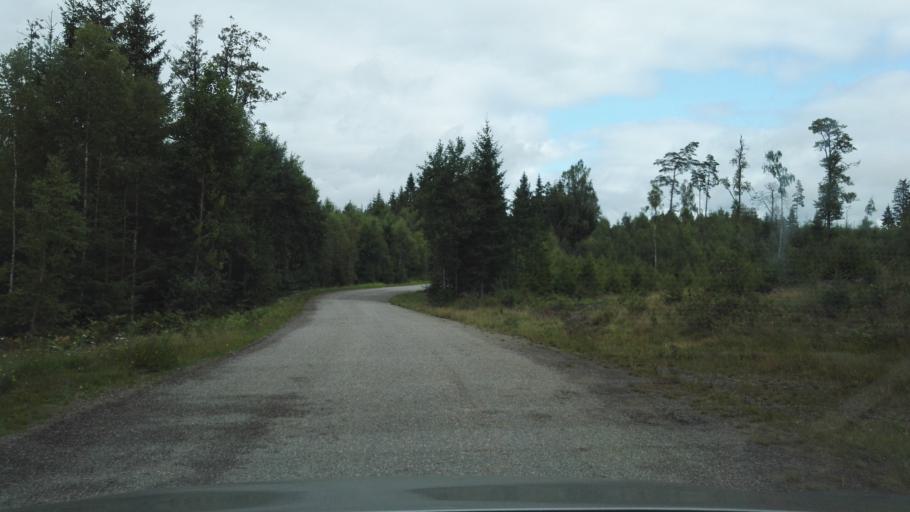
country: SE
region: Joenkoeping
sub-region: Vetlanda Kommun
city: Landsbro
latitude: 57.2062
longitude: 14.7940
